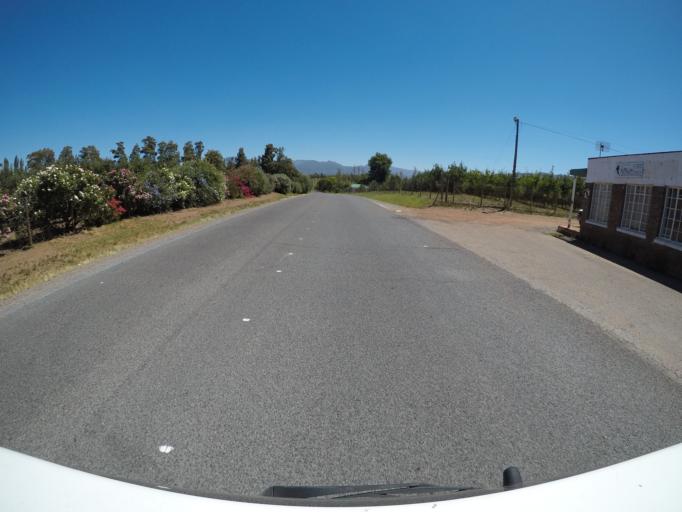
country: ZA
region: Western Cape
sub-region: Overberg District Municipality
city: Grabouw
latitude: -34.1887
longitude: 19.0399
